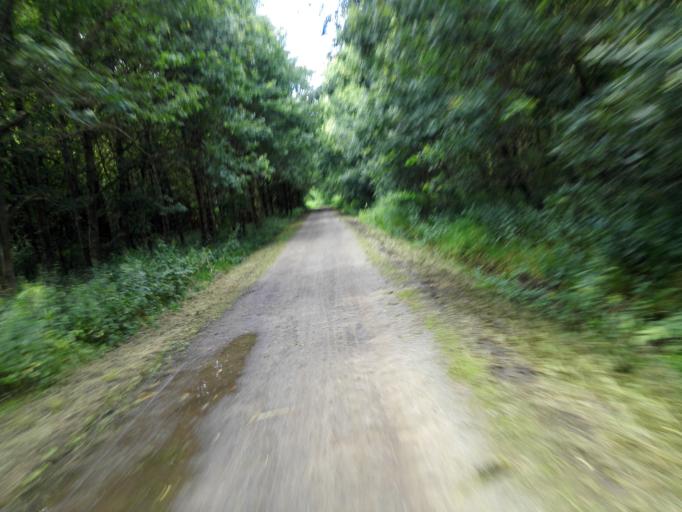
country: BE
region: Flanders
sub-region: Provincie Vlaams-Brabant
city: Tremelo
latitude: 50.9842
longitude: 4.7197
